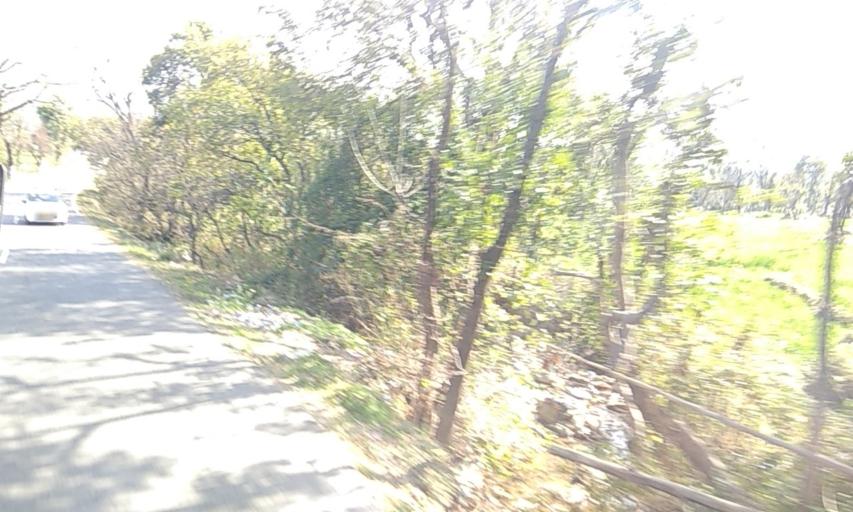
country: IN
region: Himachal Pradesh
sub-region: Kangra
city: Dharmsala
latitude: 32.1580
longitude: 76.4121
